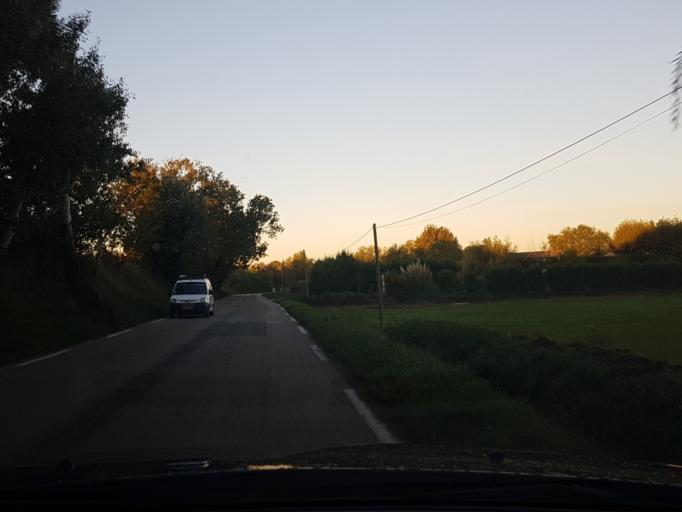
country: FR
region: Provence-Alpes-Cote d'Azur
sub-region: Departement du Vaucluse
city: Althen-des-Paluds
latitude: 44.0376
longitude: 4.9591
